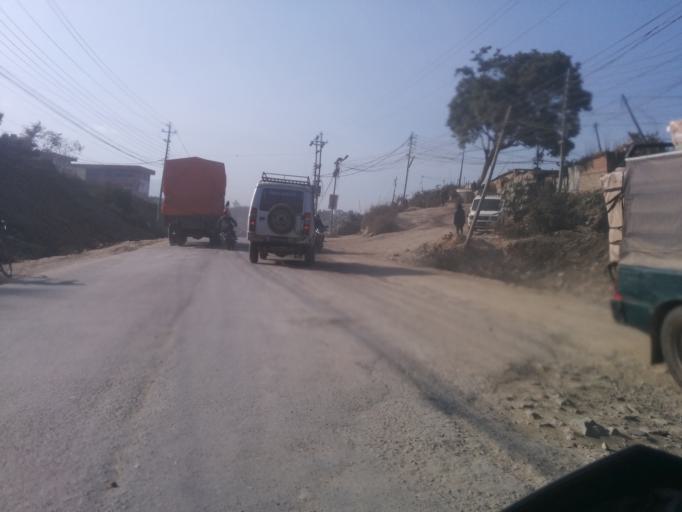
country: NP
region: Central Region
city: Kirtipur
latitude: 27.6852
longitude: 85.2951
